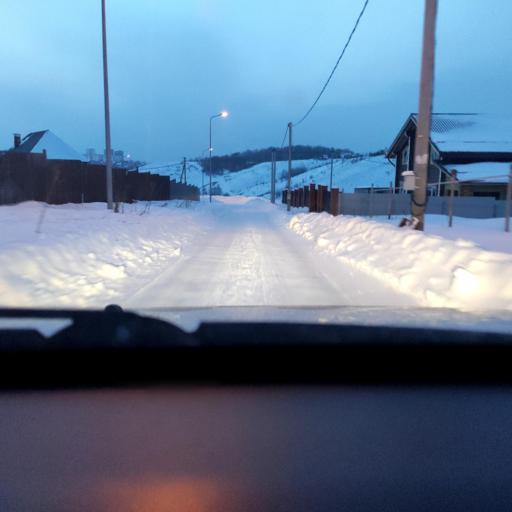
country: RU
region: Perm
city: Perm
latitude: 58.0269
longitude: 56.3579
